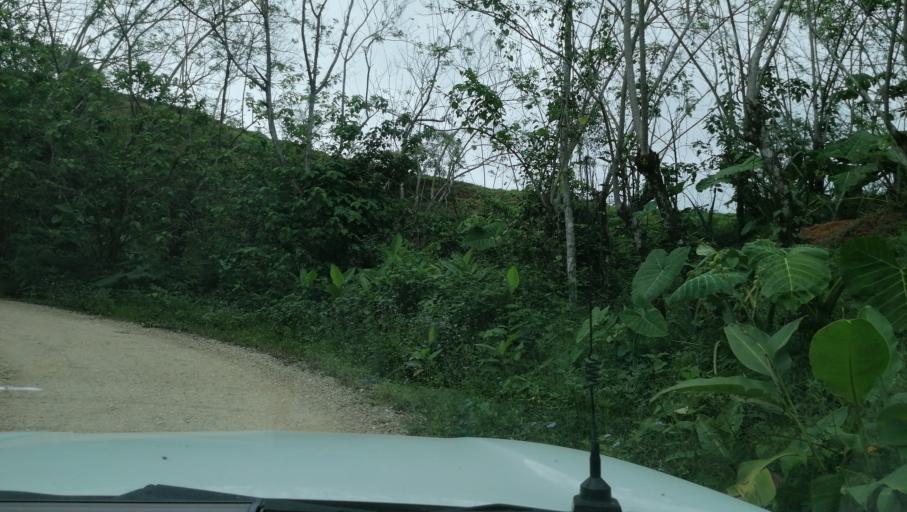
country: MX
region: Chiapas
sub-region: Ocotepec
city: San Pablo Huacano
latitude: 17.2704
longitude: -93.2453
